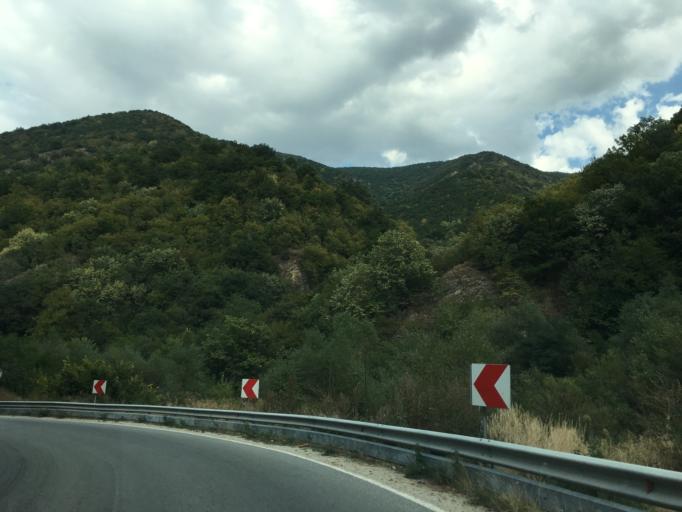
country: BG
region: Pazardzhik
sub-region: Obshtina Septemvri
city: Septemvri
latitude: 42.1286
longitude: 24.1247
